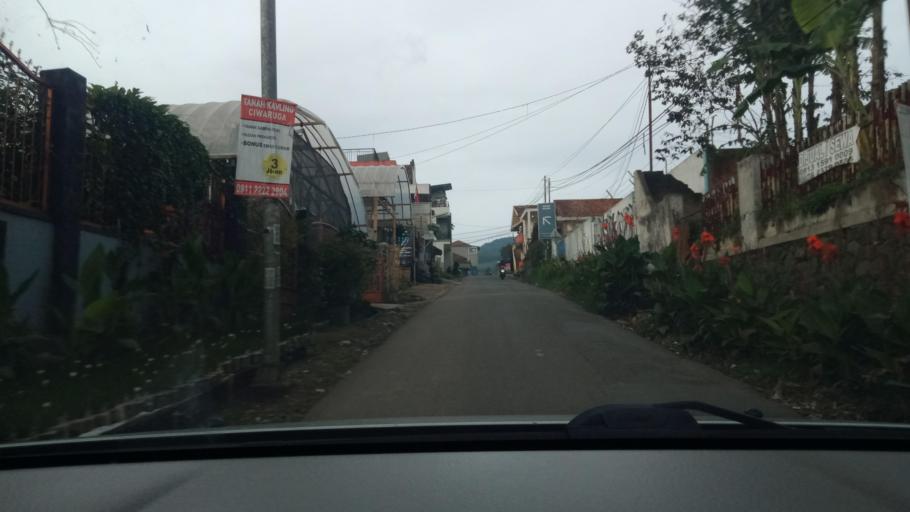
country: ID
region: West Java
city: Lembang
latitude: -6.8061
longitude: 107.5888
